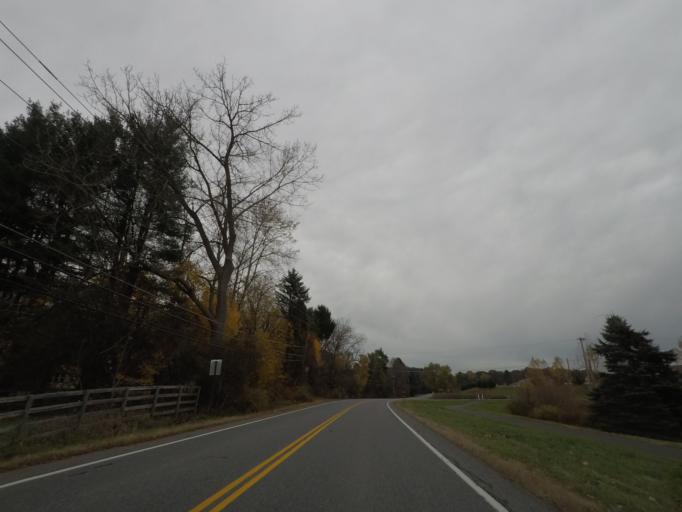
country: US
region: New York
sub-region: Schenectady County
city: Niskayuna
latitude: 42.8076
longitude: -73.8078
